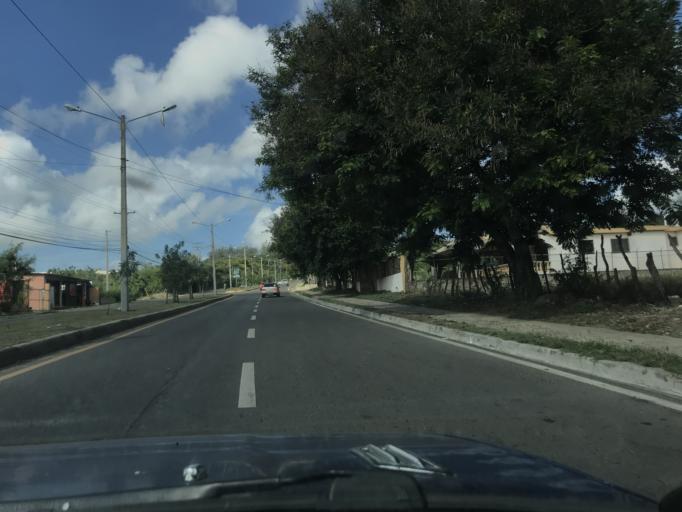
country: DO
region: Santiago
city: Santiago de los Caballeros
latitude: 19.4306
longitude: -70.7262
